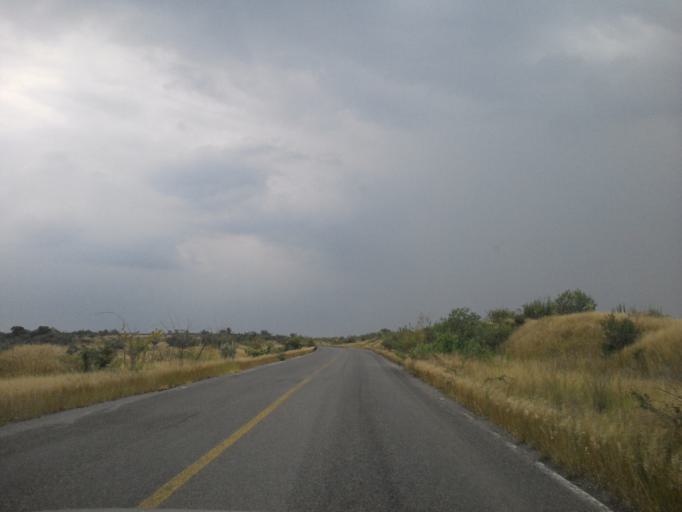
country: MX
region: Jalisco
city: San Diego de Alejandria
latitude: 20.8736
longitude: -102.0789
